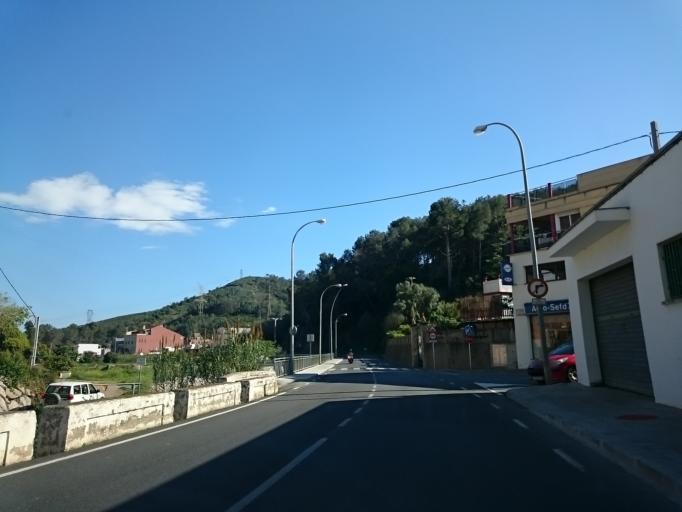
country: ES
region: Catalonia
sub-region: Provincia de Barcelona
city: Torrelles de Llobregat
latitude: 41.3354
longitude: 2.0014
